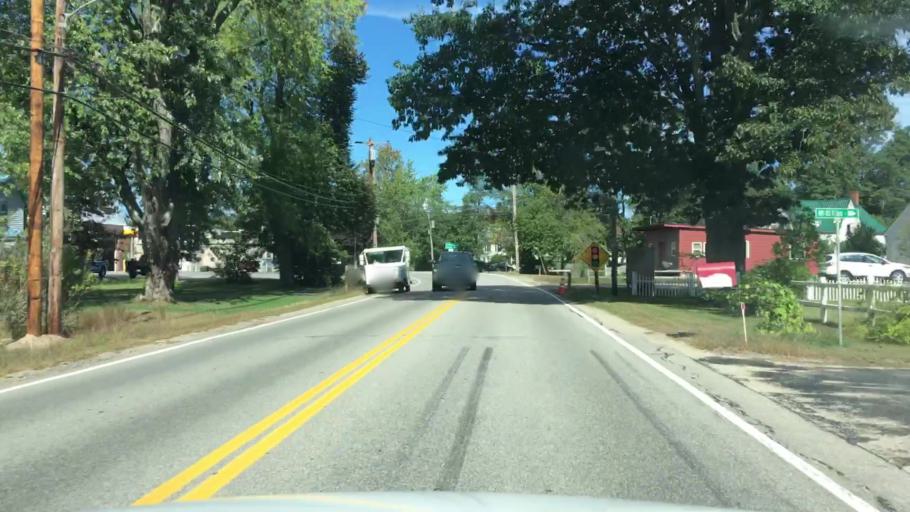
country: US
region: Maine
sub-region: Cumberland County
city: Westbrook
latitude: 43.6408
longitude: -70.3984
